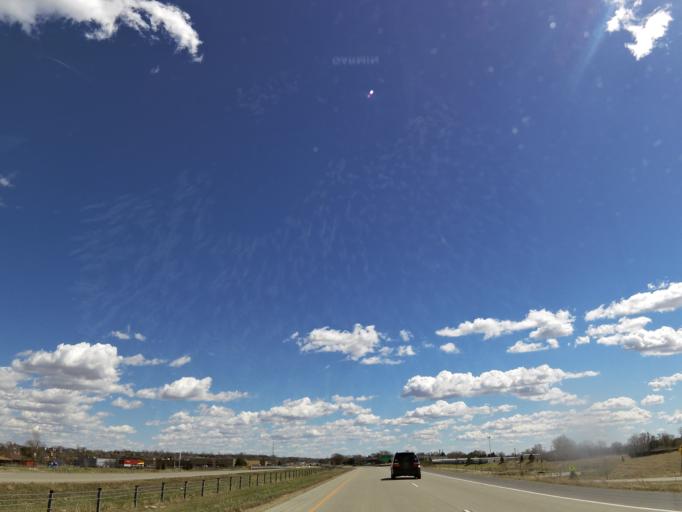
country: US
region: Minnesota
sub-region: Washington County
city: Cottage Grove
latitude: 44.8167
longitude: -92.9374
